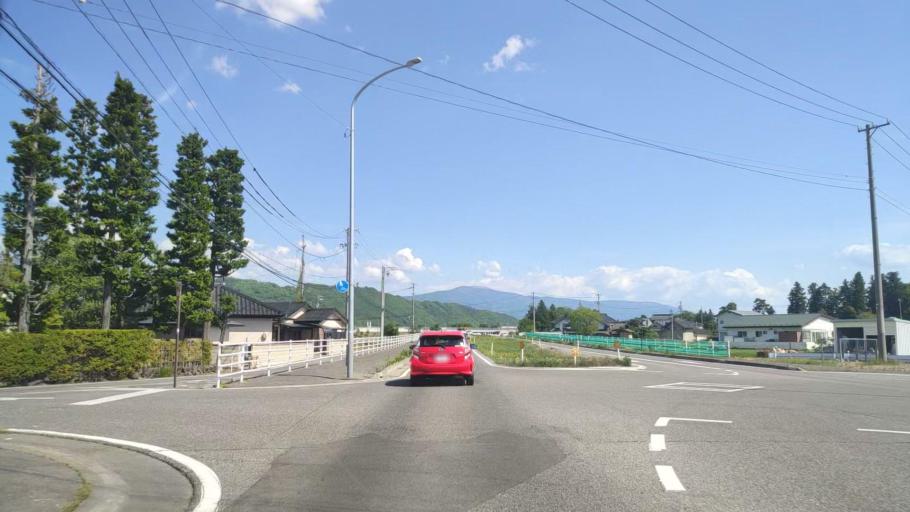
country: JP
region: Nagano
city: Toyoshina
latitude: 36.2769
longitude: 137.9260
